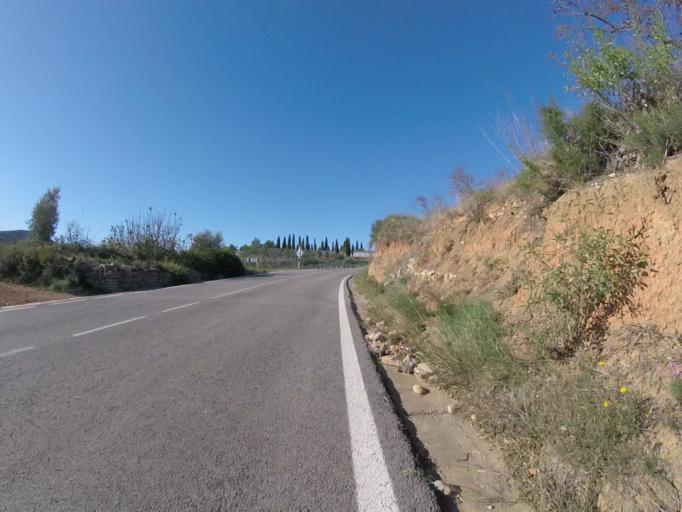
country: ES
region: Valencia
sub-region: Provincia de Castello
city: Chert/Xert
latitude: 40.4653
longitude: 0.1950
